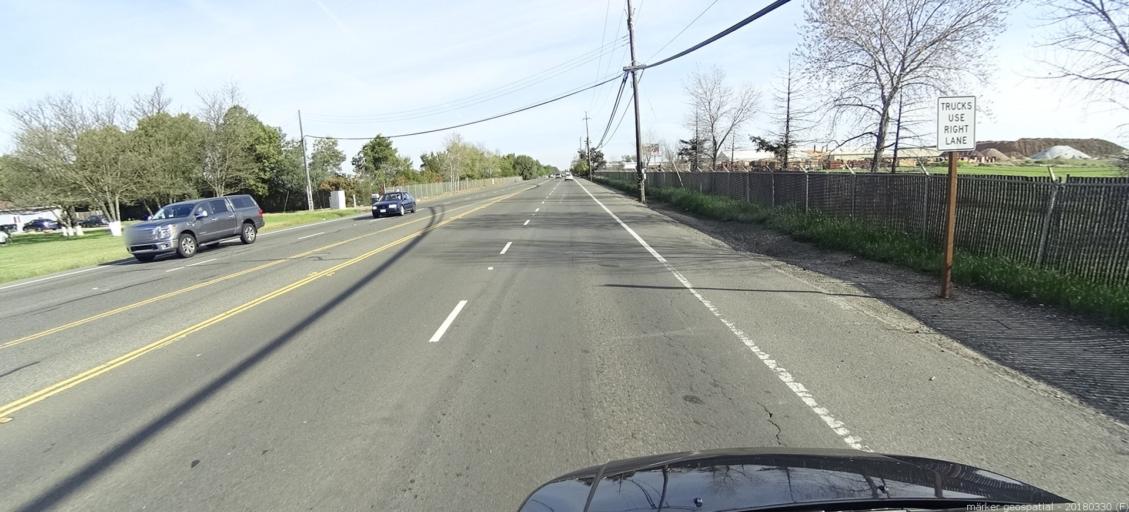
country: US
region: California
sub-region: Sacramento County
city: Rosemont
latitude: 38.5300
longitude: -121.3349
